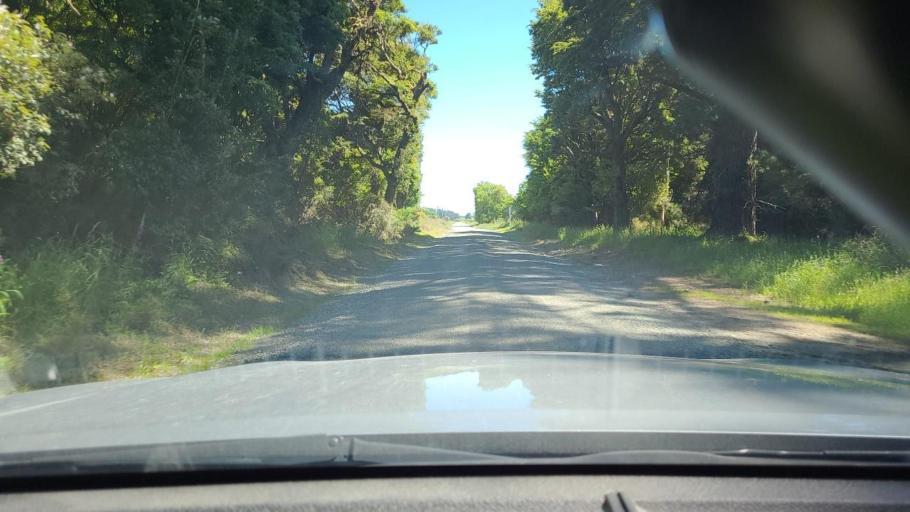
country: NZ
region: Southland
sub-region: Southland District
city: Riverton
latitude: -45.9542
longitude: 167.6733
